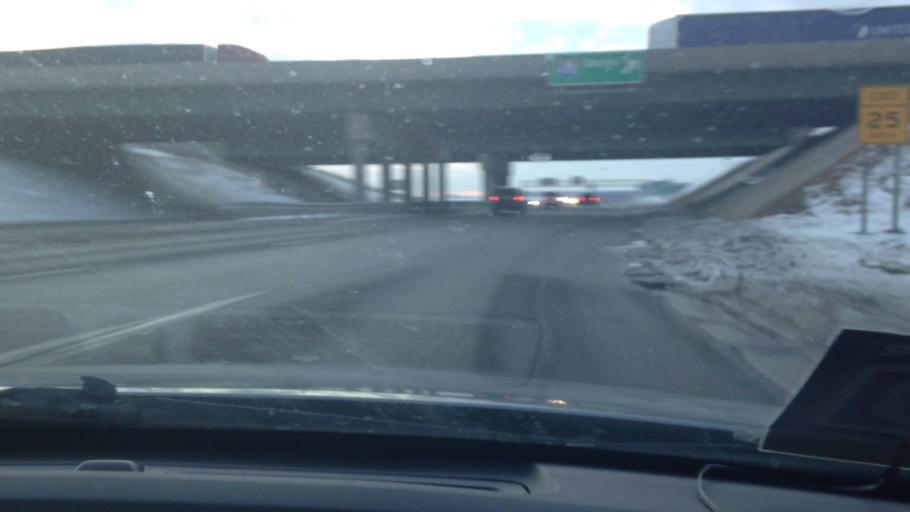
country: US
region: Kansas
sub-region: Wyandotte County
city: Edwardsville
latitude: 39.1169
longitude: -94.8093
